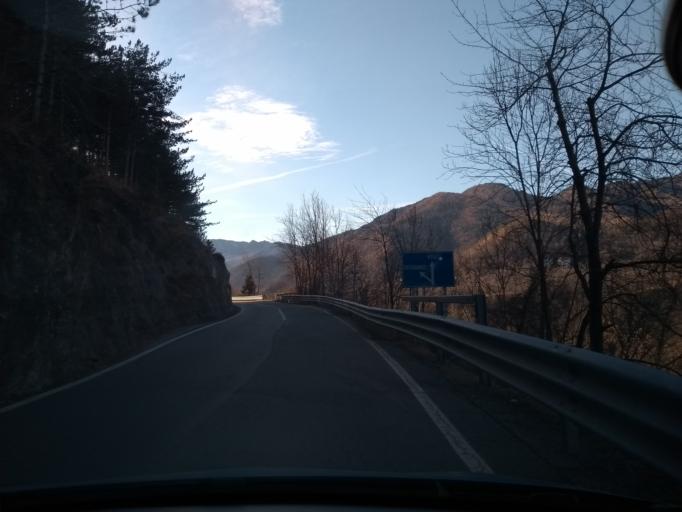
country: IT
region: Piedmont
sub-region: Provincia di Torino
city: La Villa
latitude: 45.2661
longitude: 7.4411
